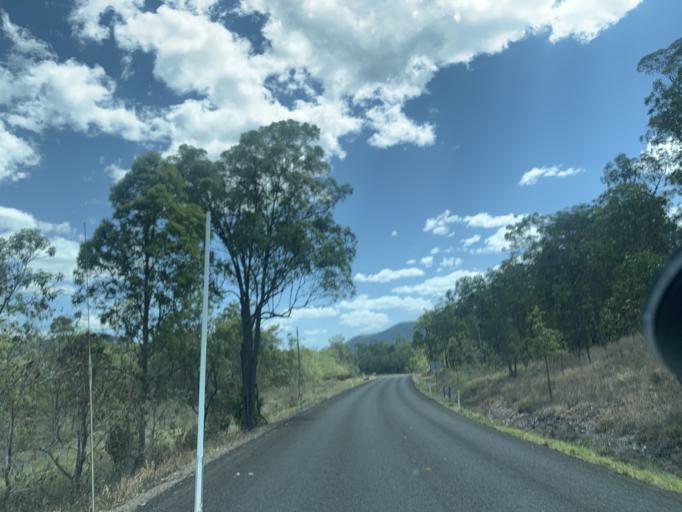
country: AU
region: Queensland
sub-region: Tablelands
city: Atherton
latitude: -17.3122
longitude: 145.4546
